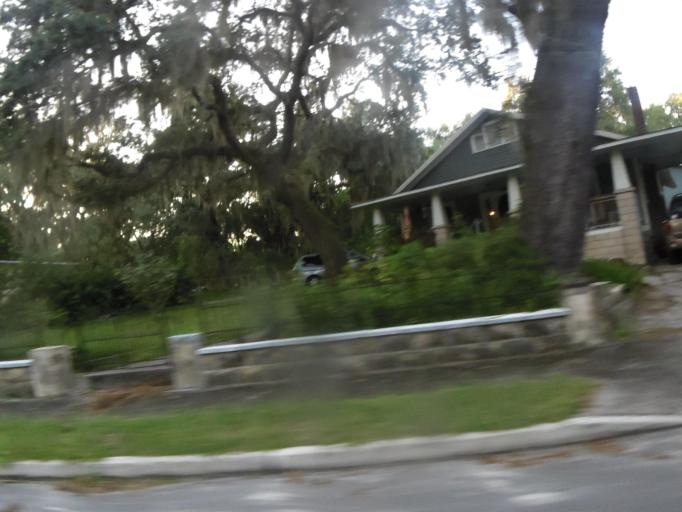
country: US
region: Florida
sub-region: Putnam County
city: Palatka
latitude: 29.6403
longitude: -81.6421
